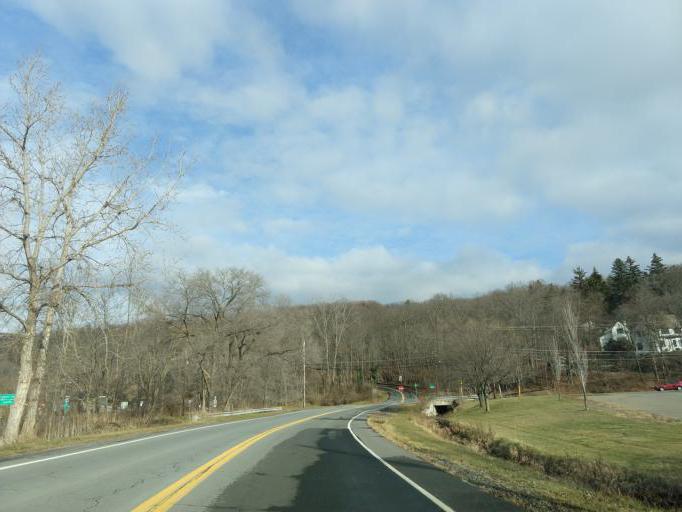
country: US
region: New York
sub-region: Tompkins County
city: Cayuga Heights
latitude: 42.4618
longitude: -76.4992
